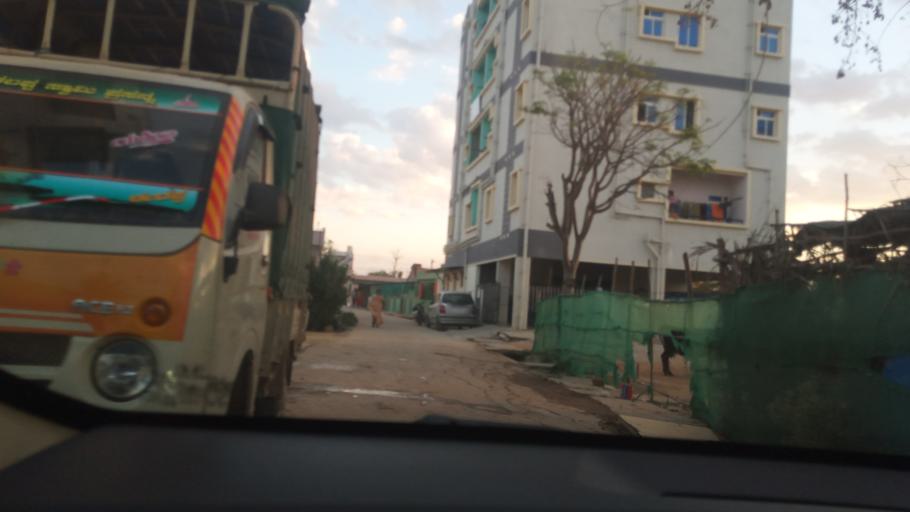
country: IN
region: Karnataka
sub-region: Bangalore Rural
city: Hoskote
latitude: 12.9788
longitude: 77.8011
